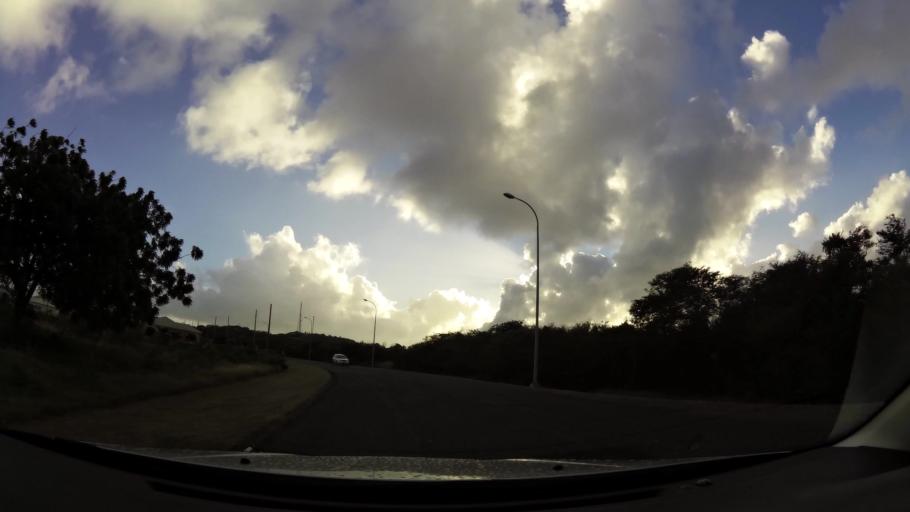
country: AG
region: Saint John
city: Saint John's
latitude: 17.1563
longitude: -61.8284
